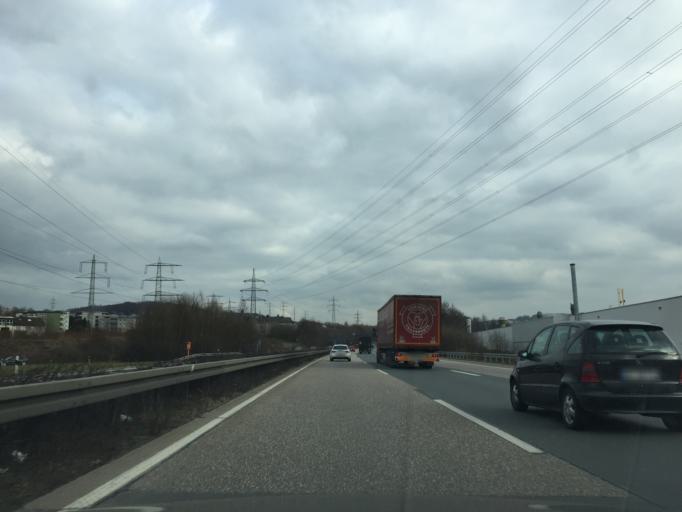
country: DE
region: North Rhine-Westphalia
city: Schwerte
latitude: 51.3687
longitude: 7.5504
